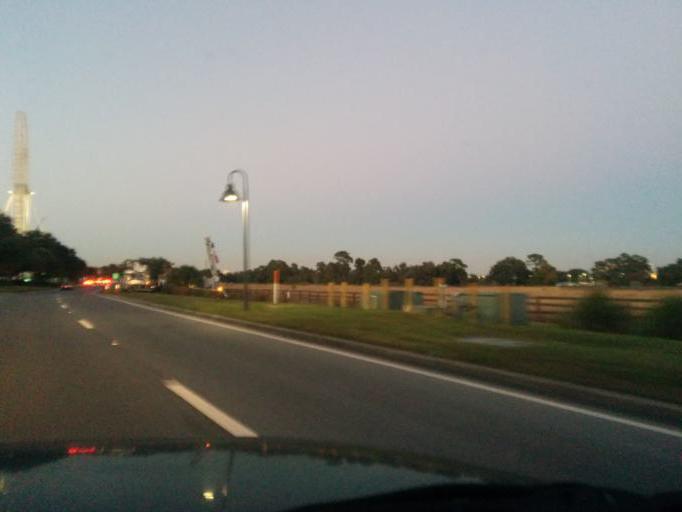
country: US
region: Florida
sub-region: Orange County
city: Doctor Phillips
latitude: 28.4392
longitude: -81.4680
